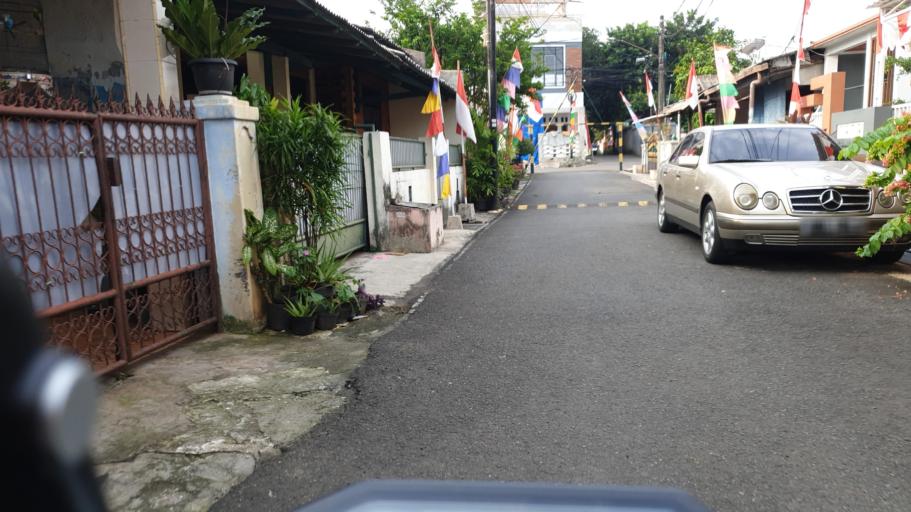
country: ID
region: West Java
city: Depok
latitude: -6.3393
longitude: 106.8305
